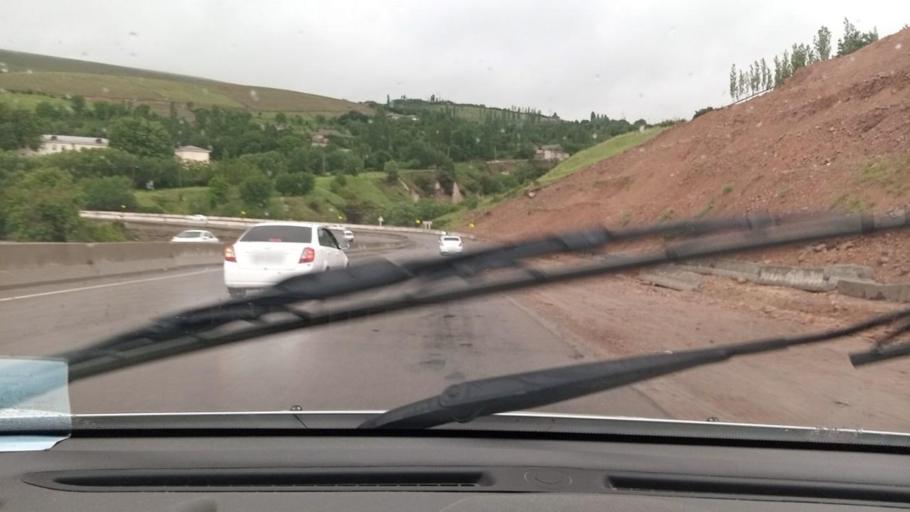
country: UZ
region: Toshkent
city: Angren
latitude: 41.0716
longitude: 70.2359
